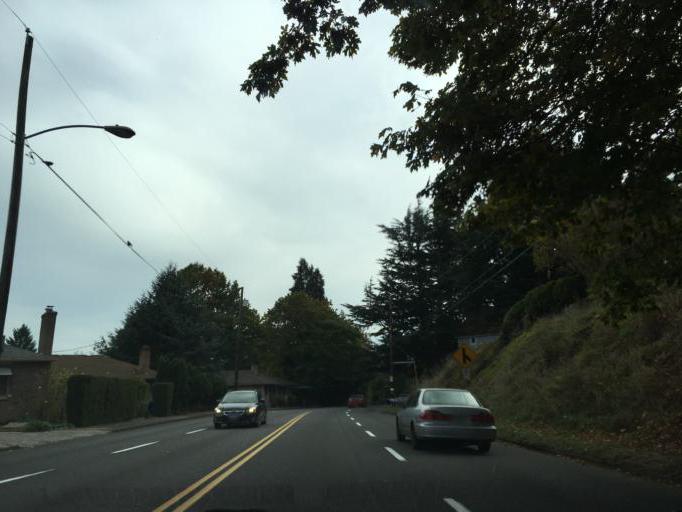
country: US
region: Oregon
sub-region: Multnomah County
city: Lents
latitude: 45.5207
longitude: -122.5888
